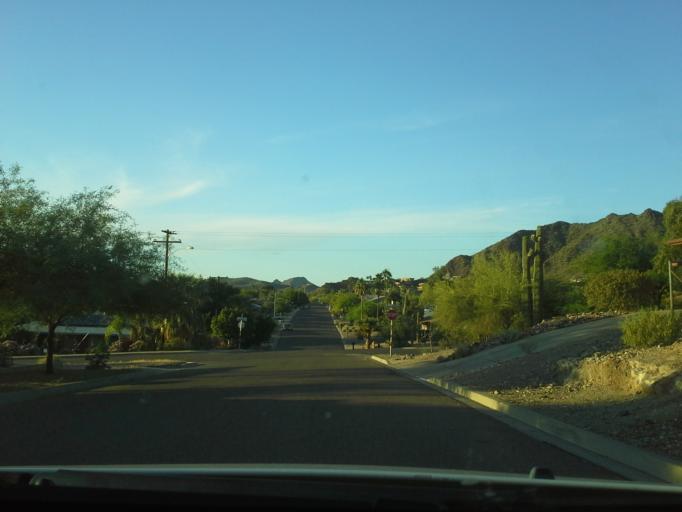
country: US
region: Arizona
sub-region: Maricopa County
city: Paradise Valley
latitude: 33.5708
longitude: -112.0481
